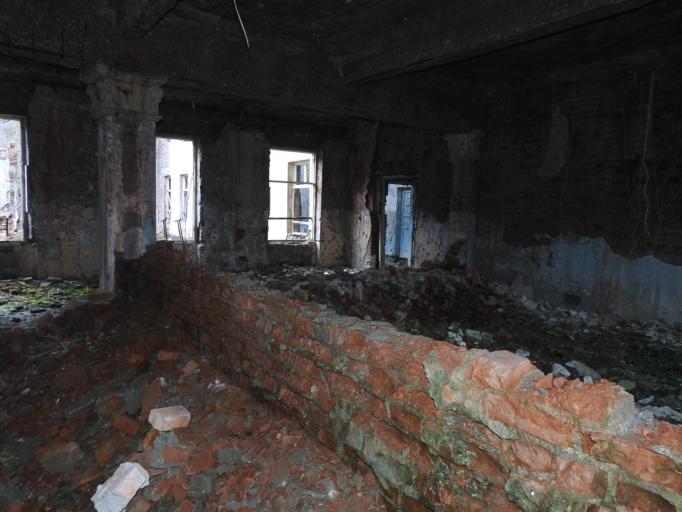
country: GE
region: Abkhazia
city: Tqvarch'eli
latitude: 42.8575
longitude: 41.7736
